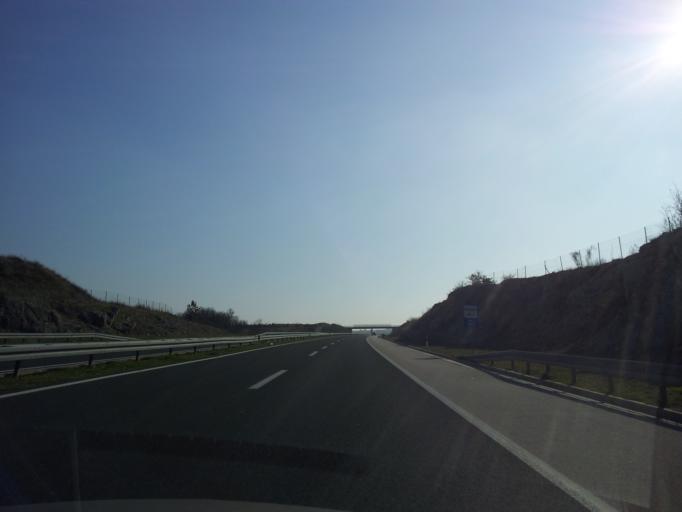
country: HR
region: Zadarska
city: Policnik
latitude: 44.1756
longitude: 15.4270
